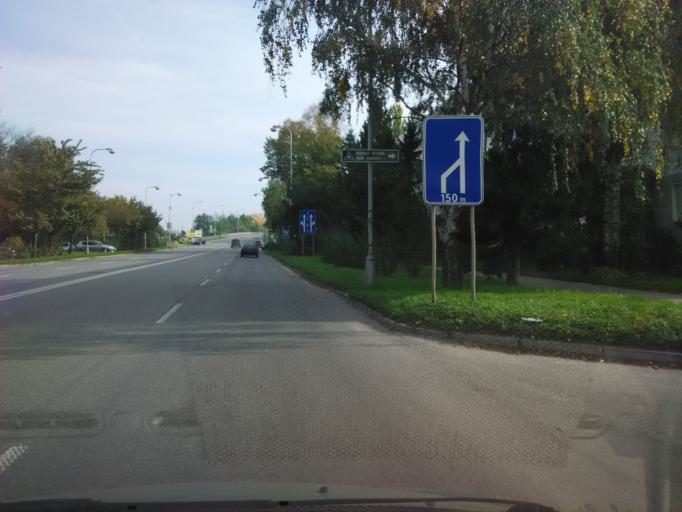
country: SK
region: Nitriansky
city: Komarno
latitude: 47.7626
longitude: 18.1372
